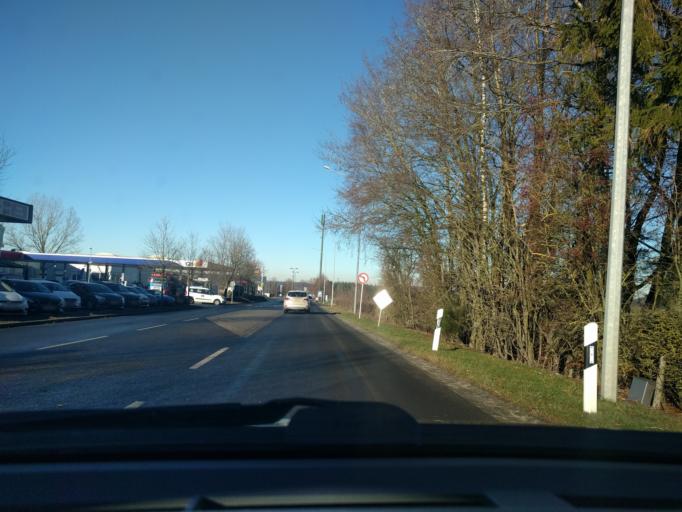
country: LU
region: Diekirch
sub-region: Canton de Clervaux
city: Troisvierges
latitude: 50.1815
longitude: 6.0235
